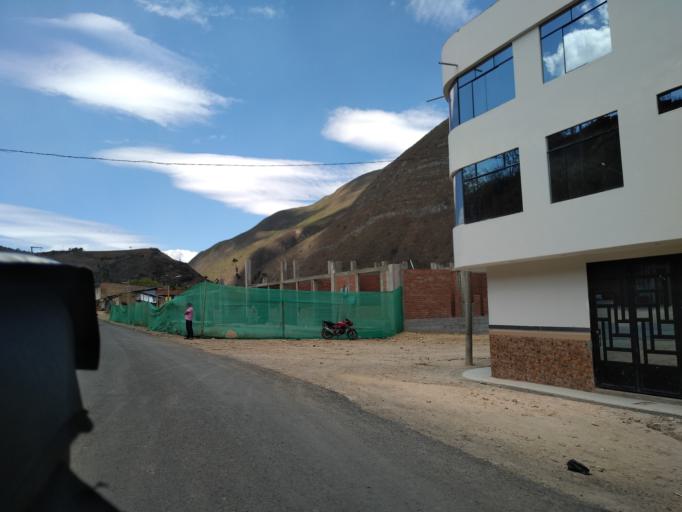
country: PE
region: Amazonas
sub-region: Provincia de Chachapoyas
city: Duraznopampa
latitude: -6.5670
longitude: -77.8290
